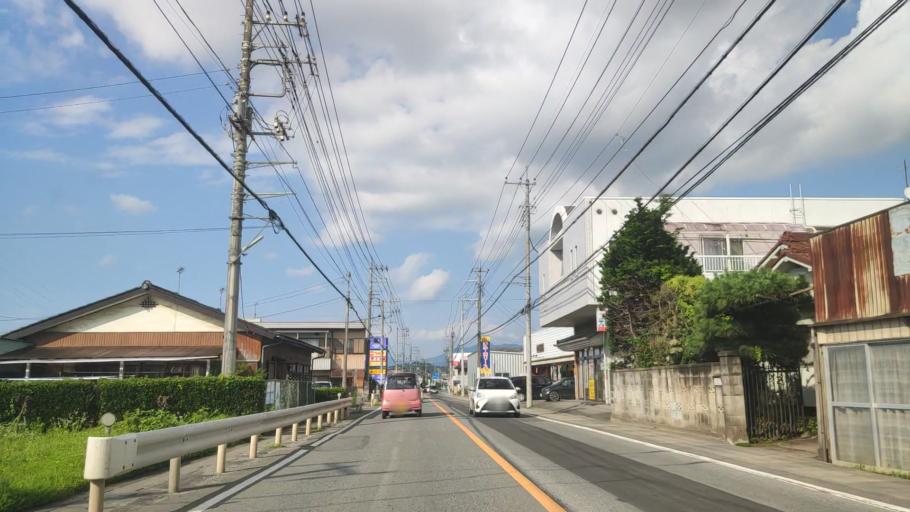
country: JP
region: Saitama
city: Chichibu
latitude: 35.9807
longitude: 139.0761
